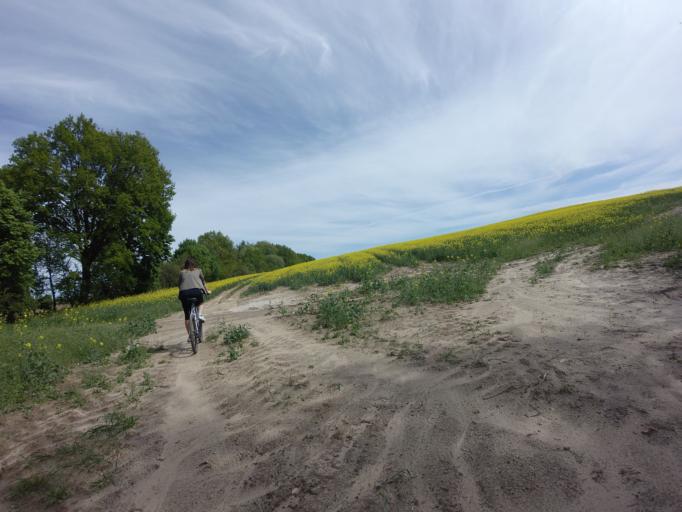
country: PL
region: West Pomeranian Voivodeship
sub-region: Powiat choszczenski
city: Recz
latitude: 53.1675
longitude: 15.5773
